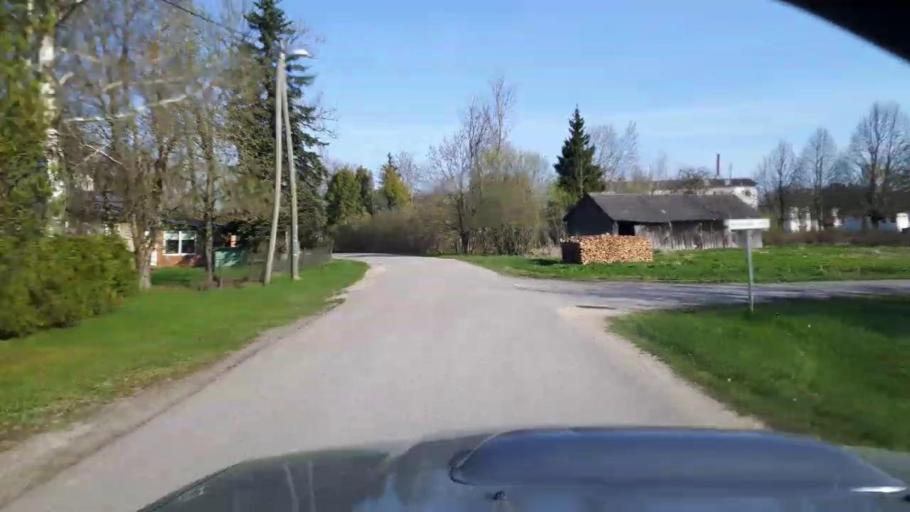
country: EE
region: Paernumaa
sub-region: Tootsi vald
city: Tootsi
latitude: 58.4943
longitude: 24.9020
